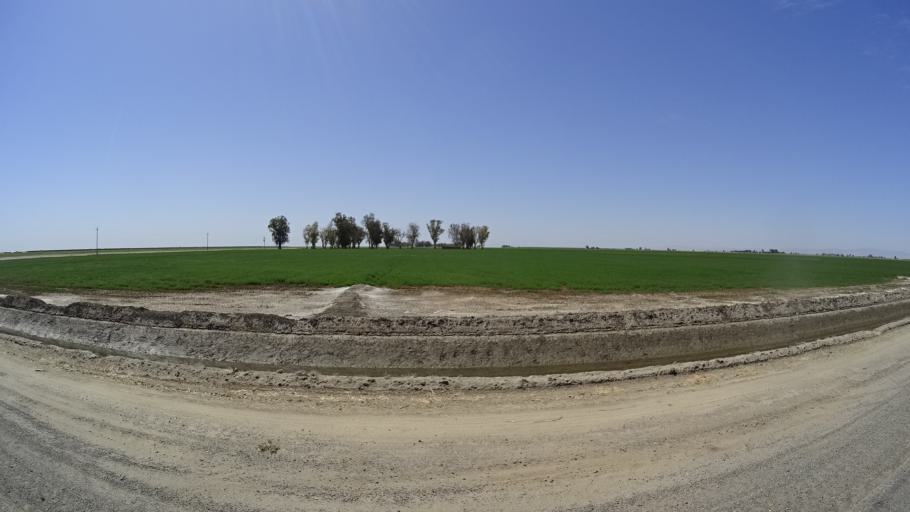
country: US
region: California
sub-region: Kings County
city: Stratford
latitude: 36.1899
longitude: -119.7642
